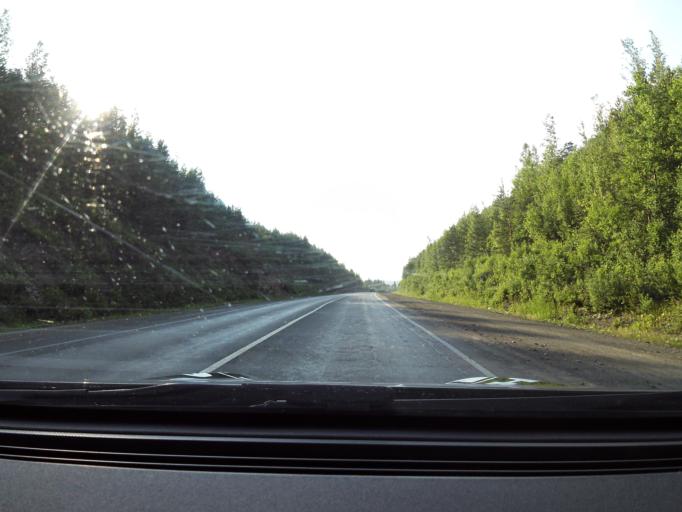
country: RU
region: Sverdlovsk
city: Revda
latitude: 56.8356
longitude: 59.8347
